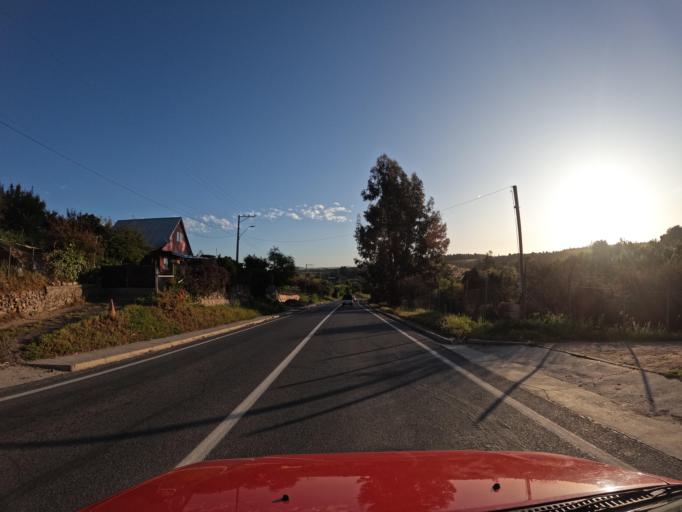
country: CL
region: O'Higgins
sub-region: Provincia de Colchagua
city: Santa Cruz
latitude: -34.2624
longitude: -71.7311
